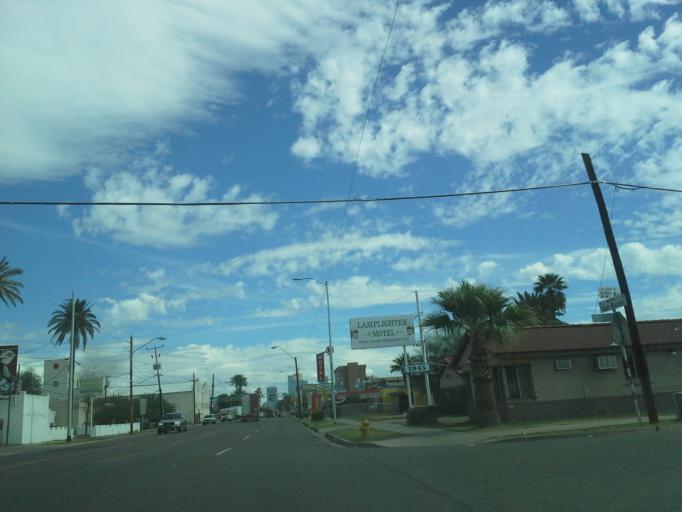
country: US
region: Arizona
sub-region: Maricopa County
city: Phoenix
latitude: 33.4512
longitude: -112.1026
